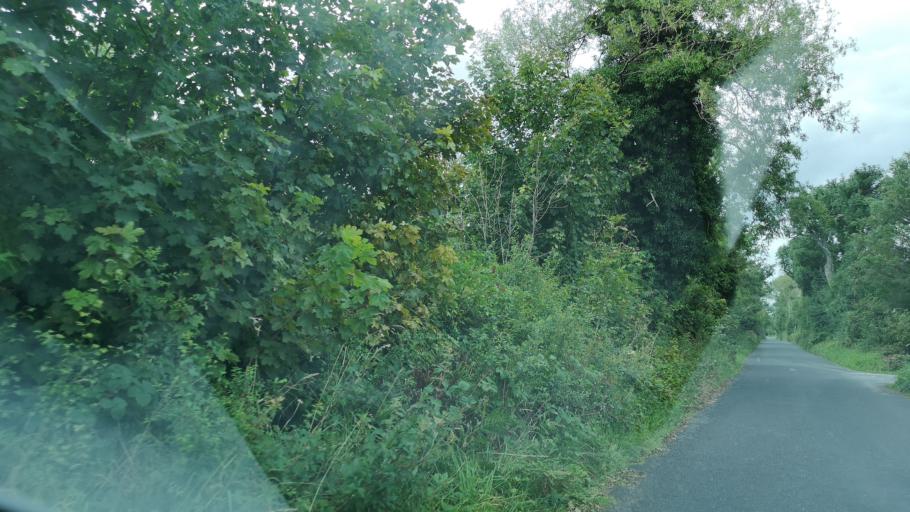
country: IE
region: Connaught
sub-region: County Galway
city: Loughrea
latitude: 53.1577
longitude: -8.4541
